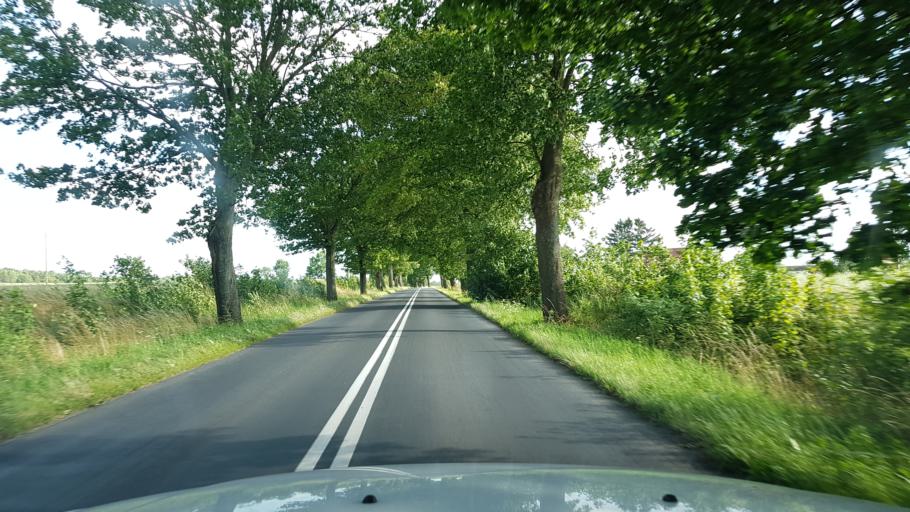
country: PL
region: West Pomeranian Voivodeship
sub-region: Powiat kolobrzeski
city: Ryman
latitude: 54.0478
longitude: 15.5453
